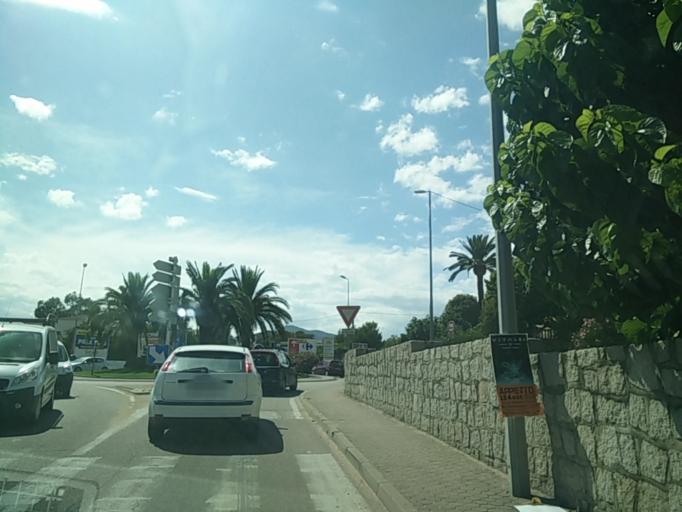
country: FR
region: Corsica
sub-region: Departement de la Corse-du-Sud
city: Afa
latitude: 41.9526
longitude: 8.7834
